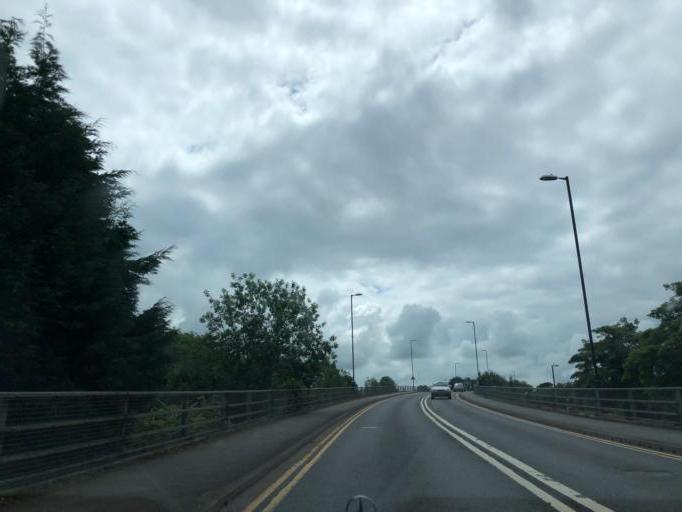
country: GB
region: England
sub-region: Solihull
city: Berkswell
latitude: 52.3968
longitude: -1.5957
